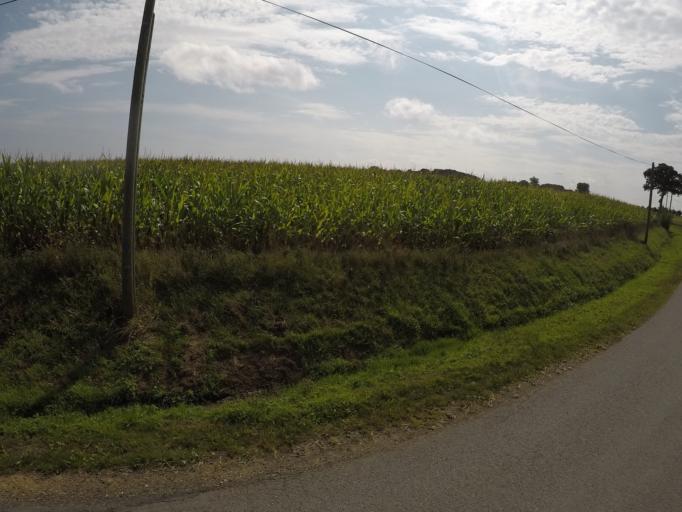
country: FR
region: Brittany
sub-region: Departement des Cotes-d'Armor
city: Goudelin
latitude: 48.6038
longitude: -2.9983
